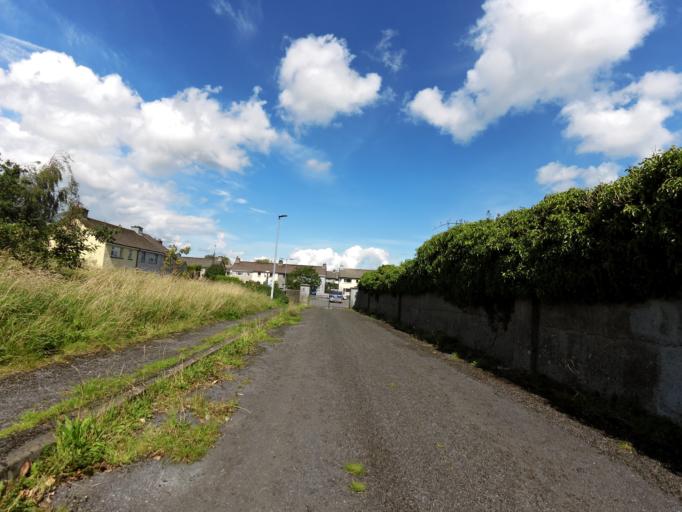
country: IE
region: Connaught
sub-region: County Galway
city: Gaillimh
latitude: 53.2741
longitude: -9.0726
